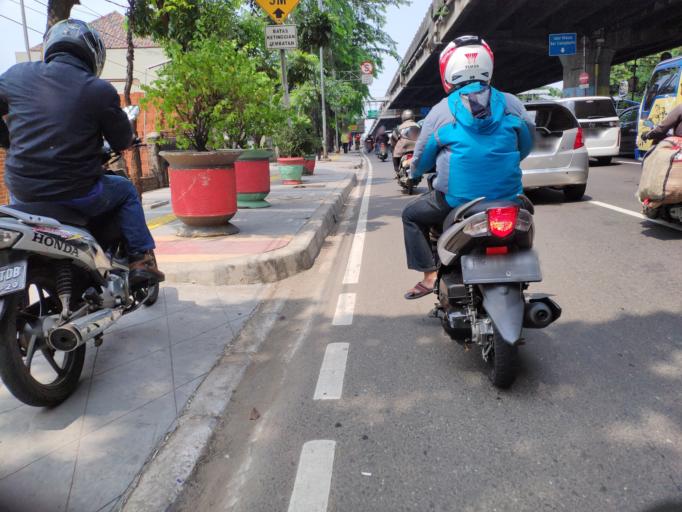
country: ID
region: Jakarta Raya
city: Jakarta
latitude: -6.1985
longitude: 106.8737
